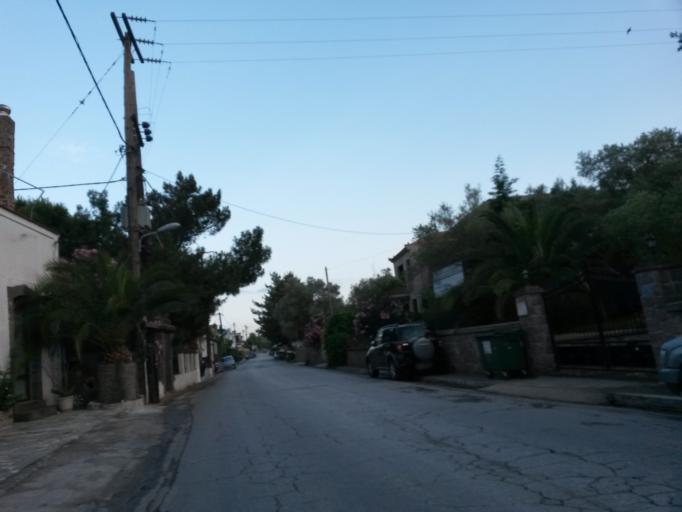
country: GR
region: North Aegean
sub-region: Nomos Lesvou
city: Pamfylla
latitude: 39.1752
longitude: 26.5021
